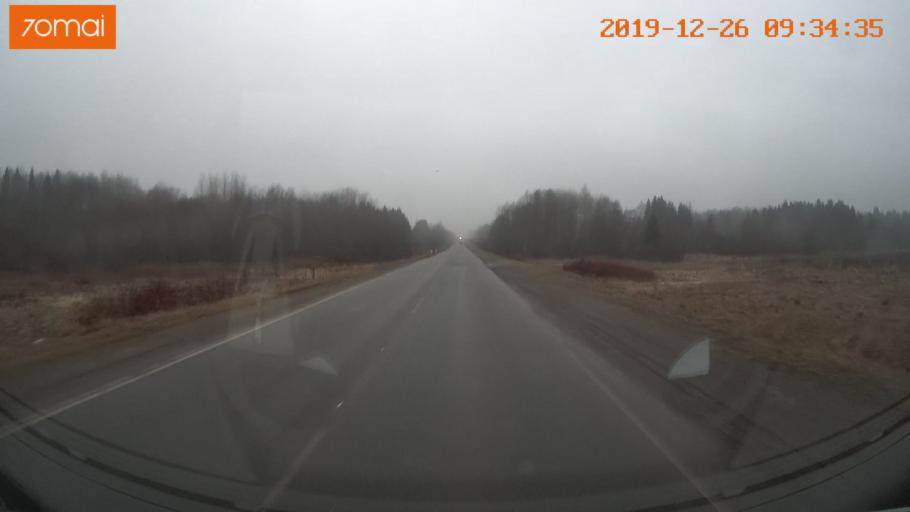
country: RU
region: Vologda
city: Vologda
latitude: 59.1034
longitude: 40.0844
